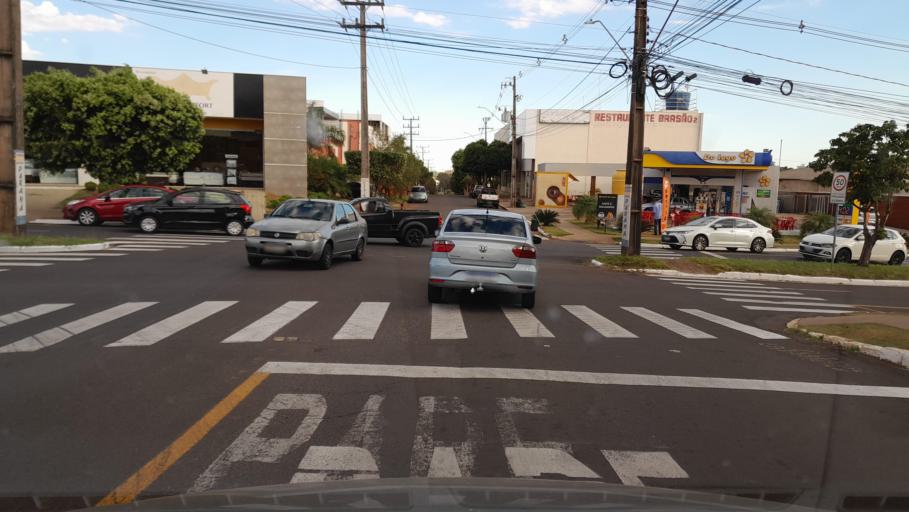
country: BR
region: Parana
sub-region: Umuarama
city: Umuarama
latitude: -23.7547
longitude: -53.2833
